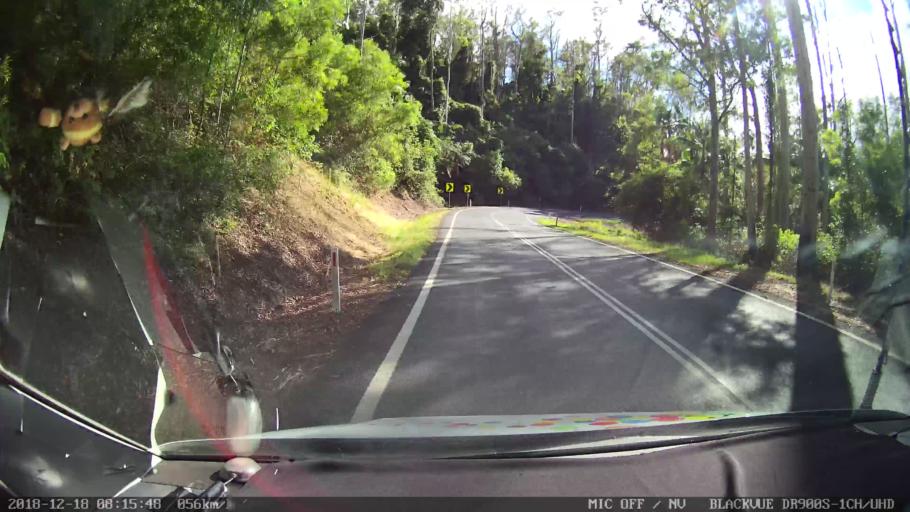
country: AU
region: New South Wales
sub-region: Kyogle
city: Kyogle
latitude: -28.3367
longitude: 152.6883
